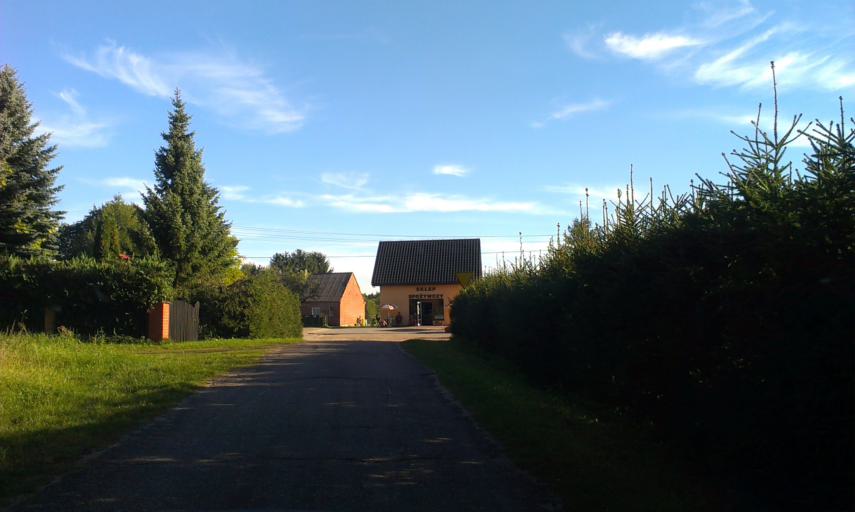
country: PL
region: West Pomeranian Voivodeship
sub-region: Powiat szczecinecki
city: Szczecinek
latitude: 53.8452
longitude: 16.6759
